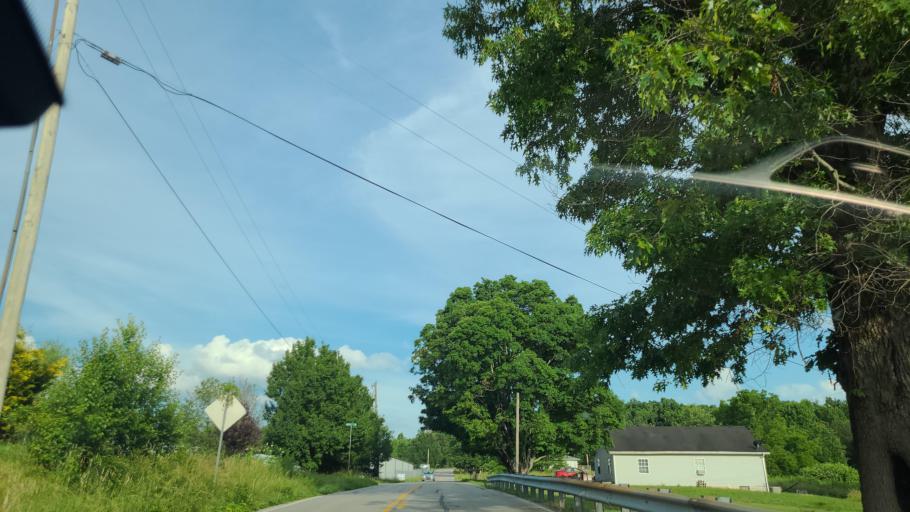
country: US
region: Kentucky
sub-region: Whitley County
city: Corbin
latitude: 36.9075
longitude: -84.2440
